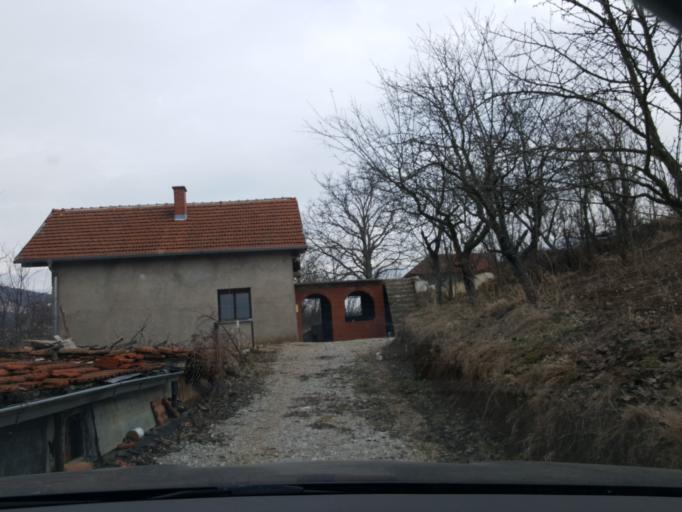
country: RS
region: Central Serbia
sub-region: Pirotski Okrug
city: Dimitrovgrad
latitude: 43.0058
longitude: 22.7560
